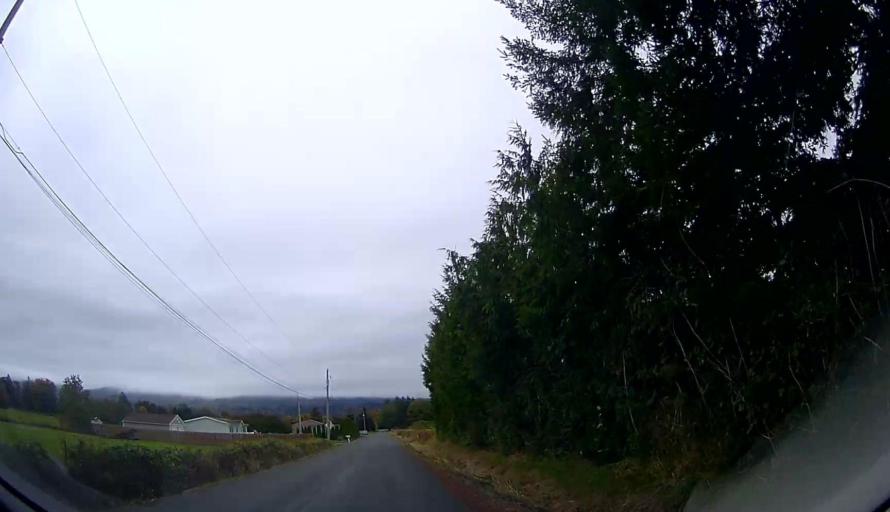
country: US
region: Washington
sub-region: Skagit County
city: Sedro-Woolley
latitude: 48.5136
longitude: -122.1721
